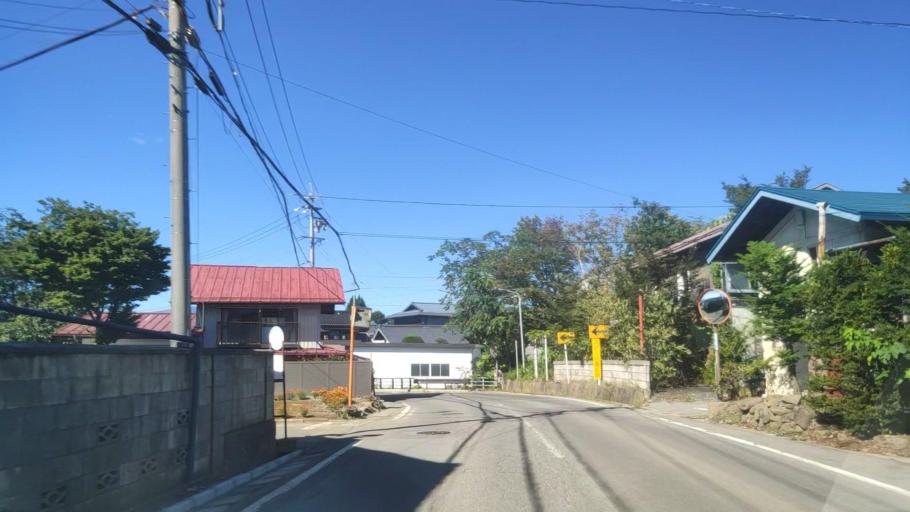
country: JP
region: Nagano
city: Chino
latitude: 35.9802
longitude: 138.2197
